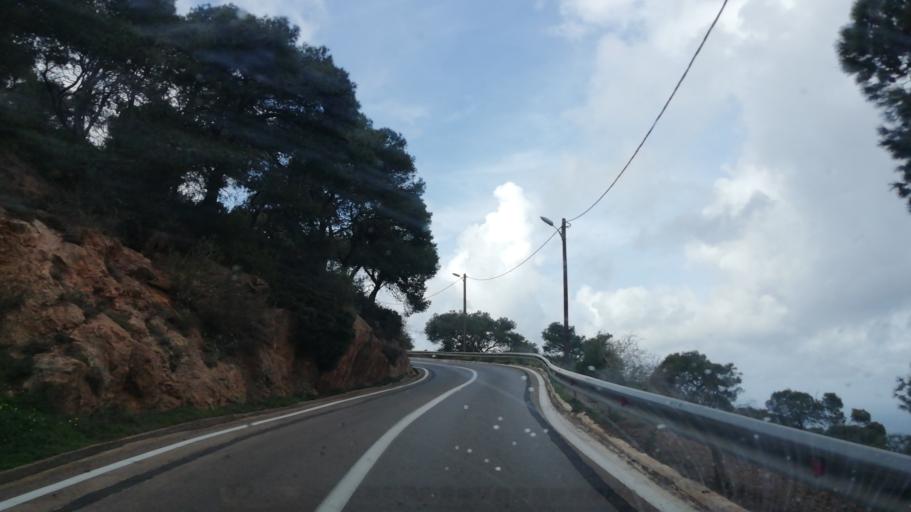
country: DZ
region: Oran
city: Oran
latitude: 35.7106
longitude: -0.6622
